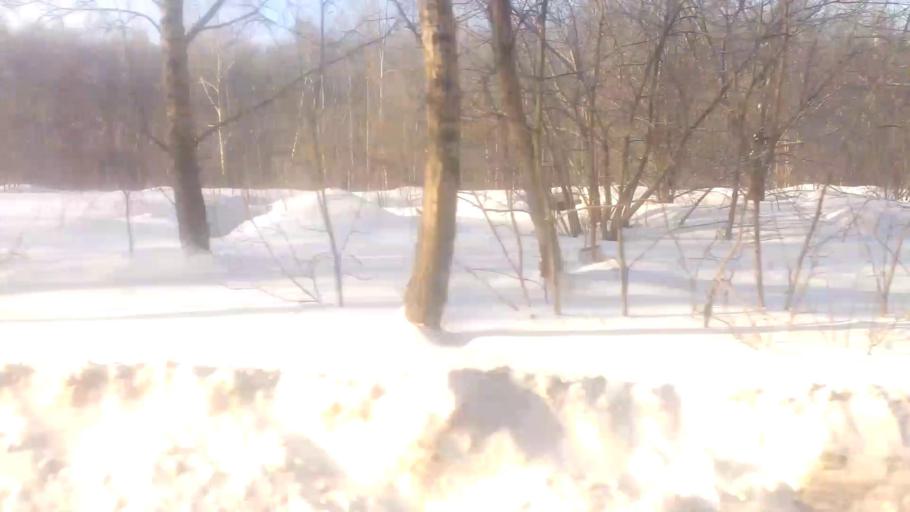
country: RU
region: Altai Krai
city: Novosilikatnyy
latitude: 53.3705
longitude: 83.6619
